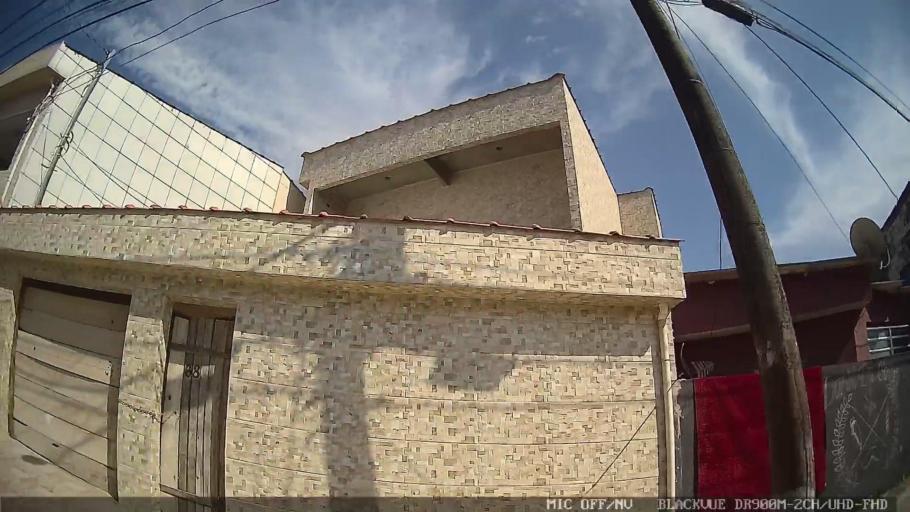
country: BR
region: Sao Paulo
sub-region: Santos
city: Santos
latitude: -23.9464
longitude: -46.2861
